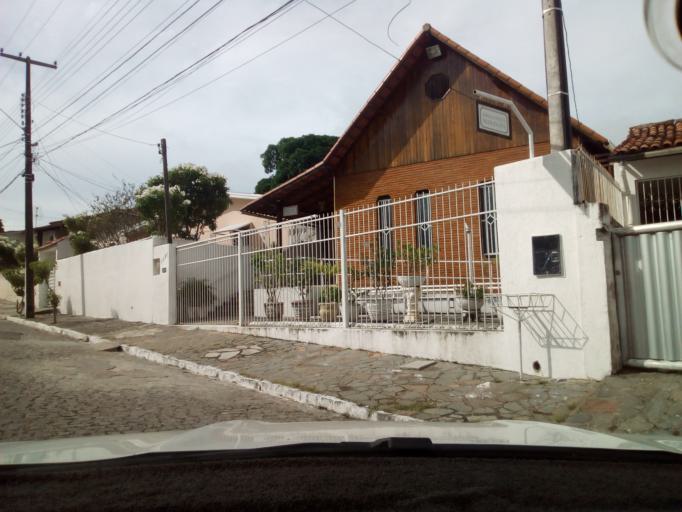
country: BR
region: Paraiba
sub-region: Joao Pessoa
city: Joao Pessoa
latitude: -7.1274
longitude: -34.8566
